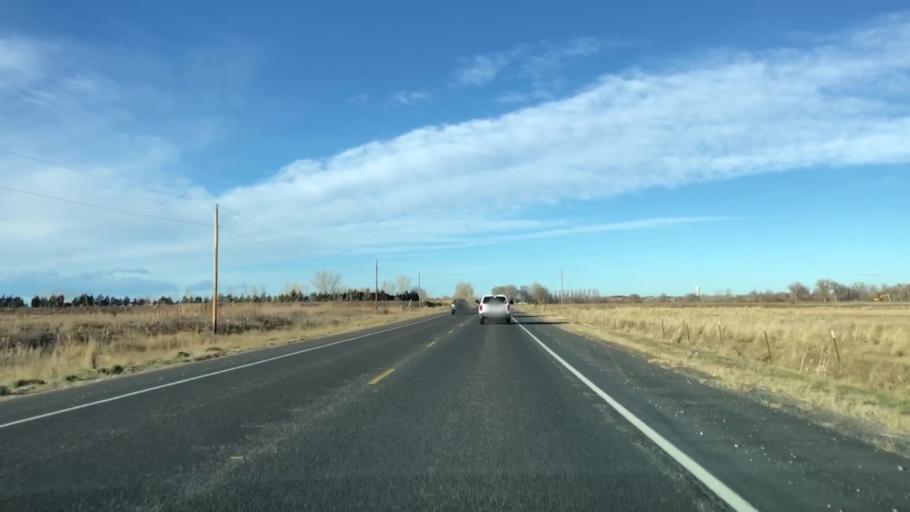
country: US
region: Colorado
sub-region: Weld County
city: Windsor
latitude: 40.4994
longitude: -104.9818
